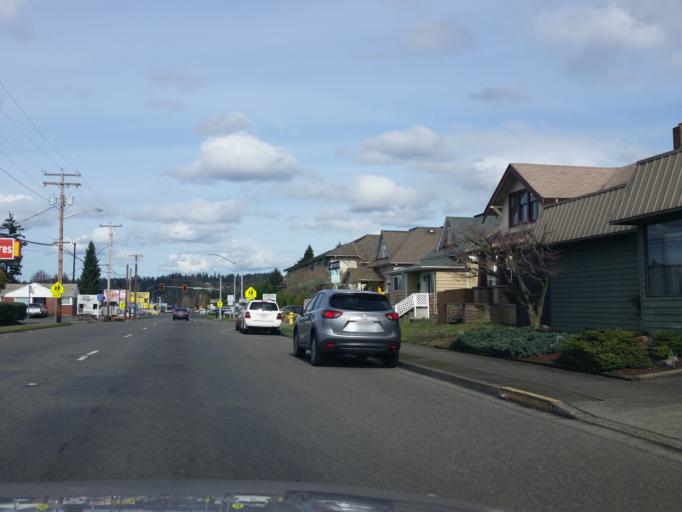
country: US
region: Washington
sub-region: Pierce County
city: Puyallup
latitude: 47.1943
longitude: -122.2922
